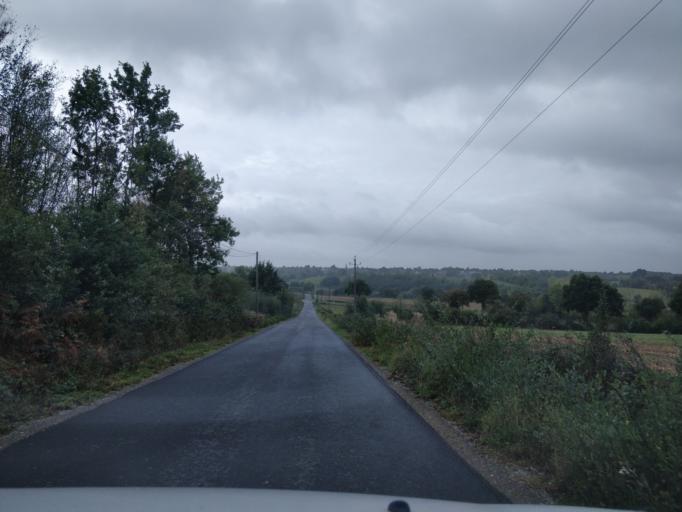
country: FR
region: Brittany
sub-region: Departement d'Ille-et-Vilaine
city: La Bouexiere
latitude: 48.2007
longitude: -1.4354
